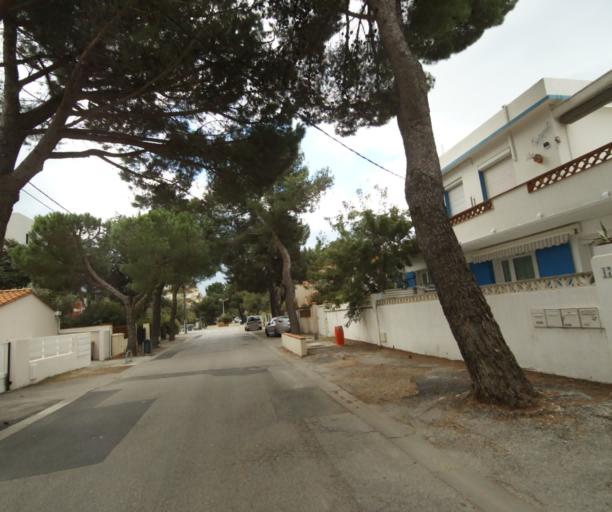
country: FR
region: Languedoc-Roussillon
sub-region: Departement des Pyrenees-Orientales
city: Argelers
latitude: 42.5601
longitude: 3.0456
